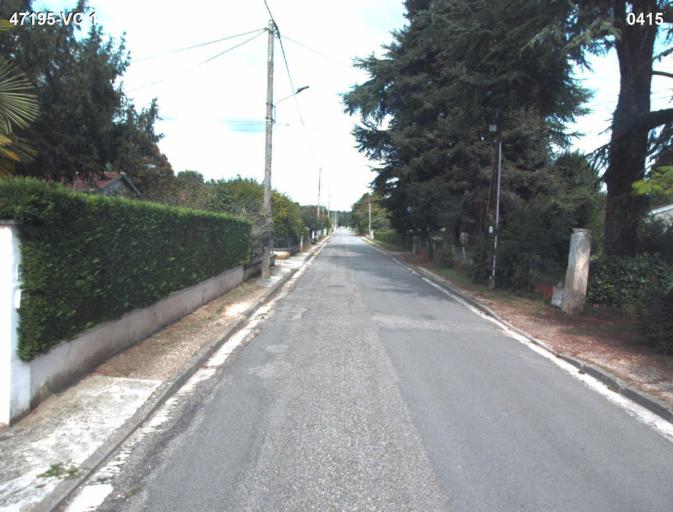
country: FR
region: Aquitaine
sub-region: Departement du Lot-et-Garonne
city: Nerac
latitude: 44.1293
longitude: 0.3445
